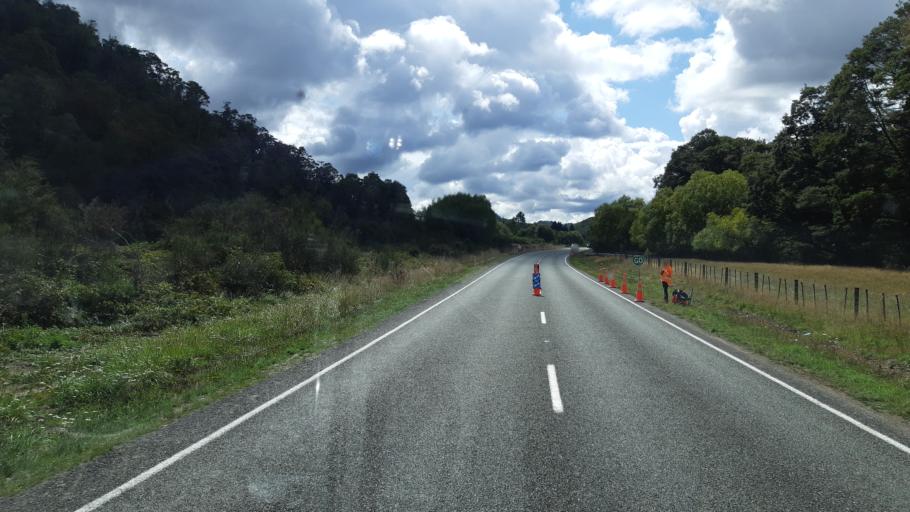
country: NZ
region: Tasman
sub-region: Tasman District
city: Wakefield
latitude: -41.6525
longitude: 172.6463
